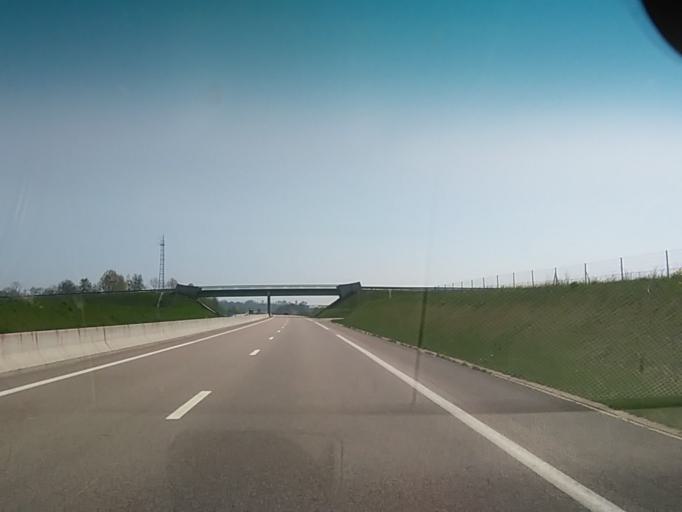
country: FR
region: Lower Normandy
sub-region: Departement de l'Orne
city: Argentan
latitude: 48.6922
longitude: -0.0131
